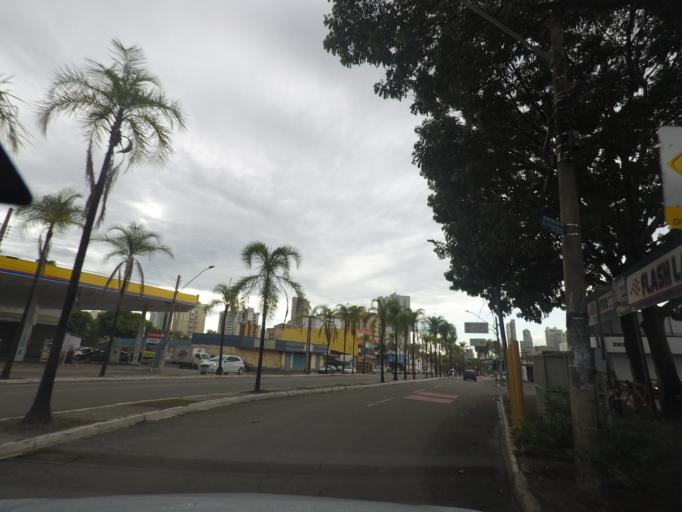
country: BR
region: Goias
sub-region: Goiania
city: Goiania
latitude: -16.7131
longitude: -49.2529
